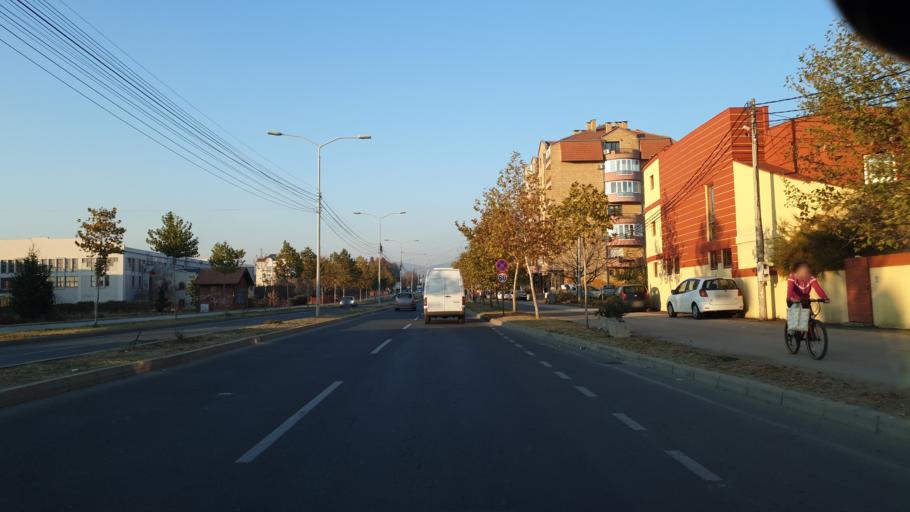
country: RS
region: Central Serbia
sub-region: Nisavski Okrug
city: Nis
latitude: 43.3269
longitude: 21.9374
